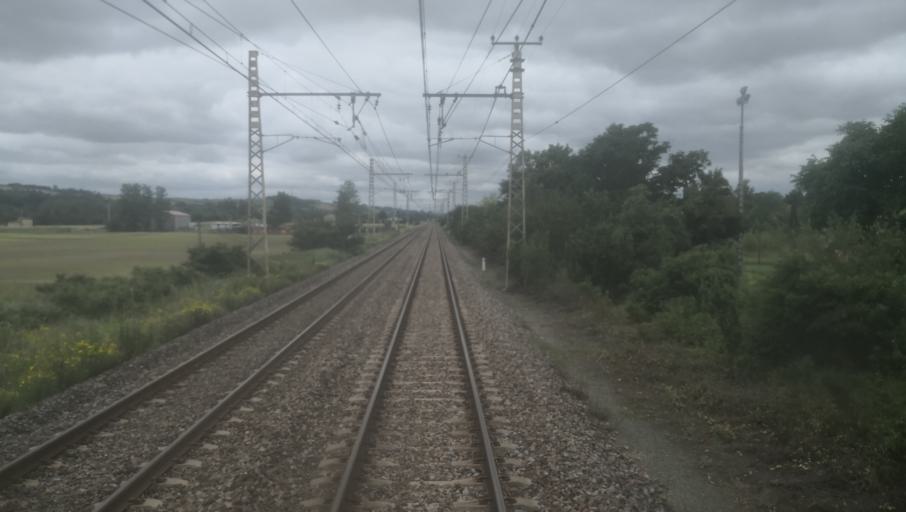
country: FR
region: Midi-Pyrenees
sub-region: Departement de la Haute-Garonne
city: Avignonet-Lauragais
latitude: 43.3644
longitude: 1.7855
